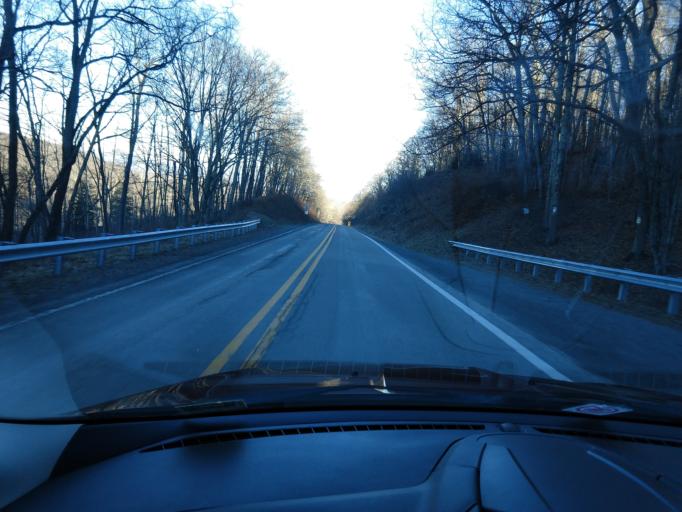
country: US
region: Virginia
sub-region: Highland County
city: Monterey
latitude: 38.4799
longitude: -79.6979
